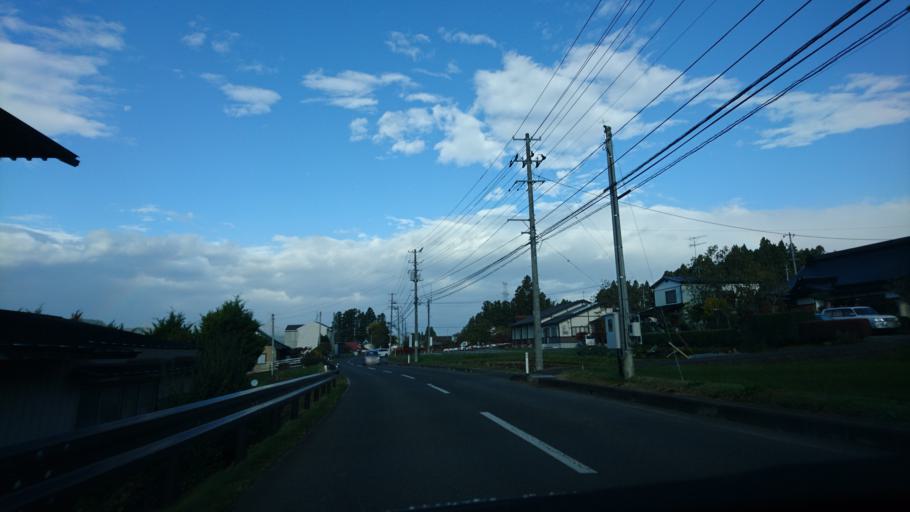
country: JP
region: Iwate
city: Ichinoseki
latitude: 39.0208
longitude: 141.0916
